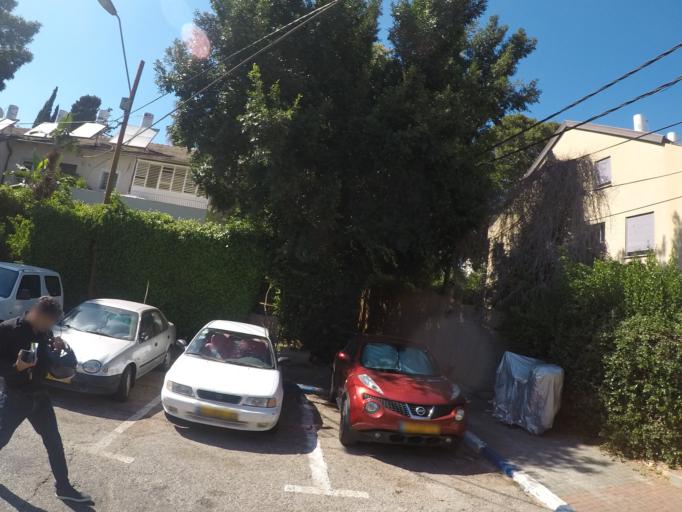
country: IL
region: Tel Aviv
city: Ramat Gan
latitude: 32.1044
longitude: 34.7969
